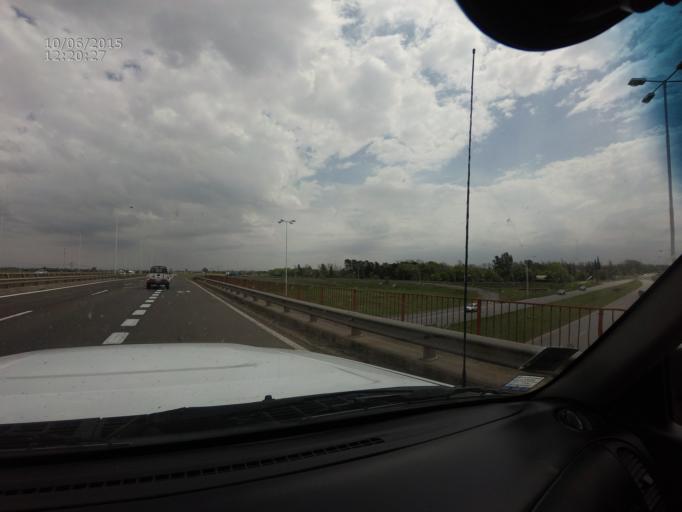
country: AR
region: Santa Fe
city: Roldan
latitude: -32.9266
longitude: -60.8998
